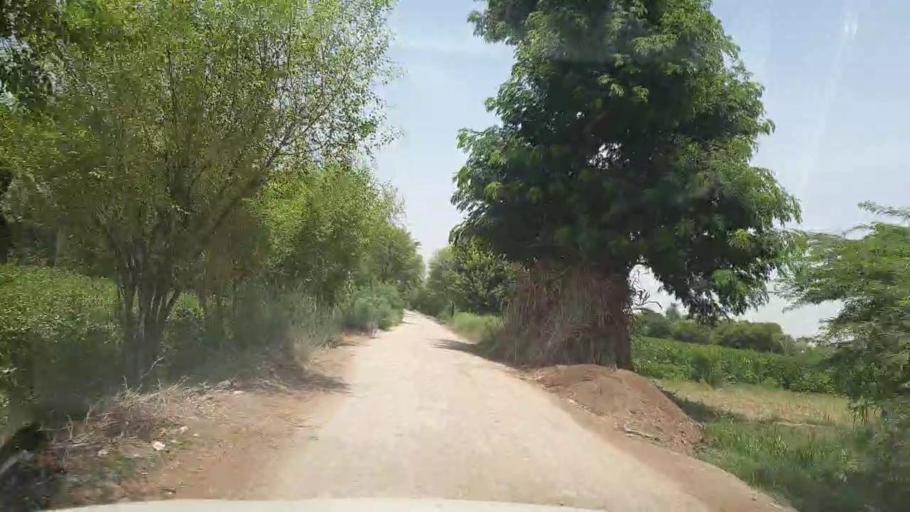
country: PK
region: Sindh
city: Bozdar
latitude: 27.1782
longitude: 68.6310
